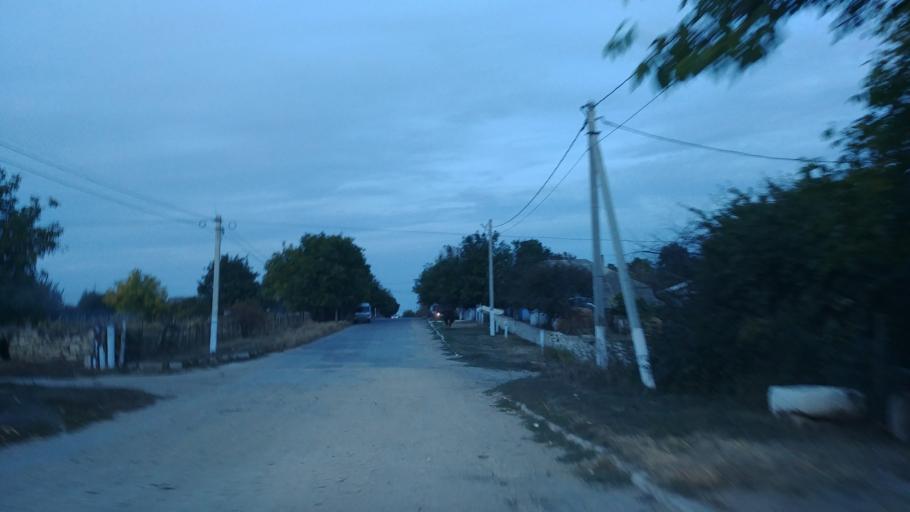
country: MD
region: Rezina
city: Saharna
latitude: 47.6724
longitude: 28.9532
